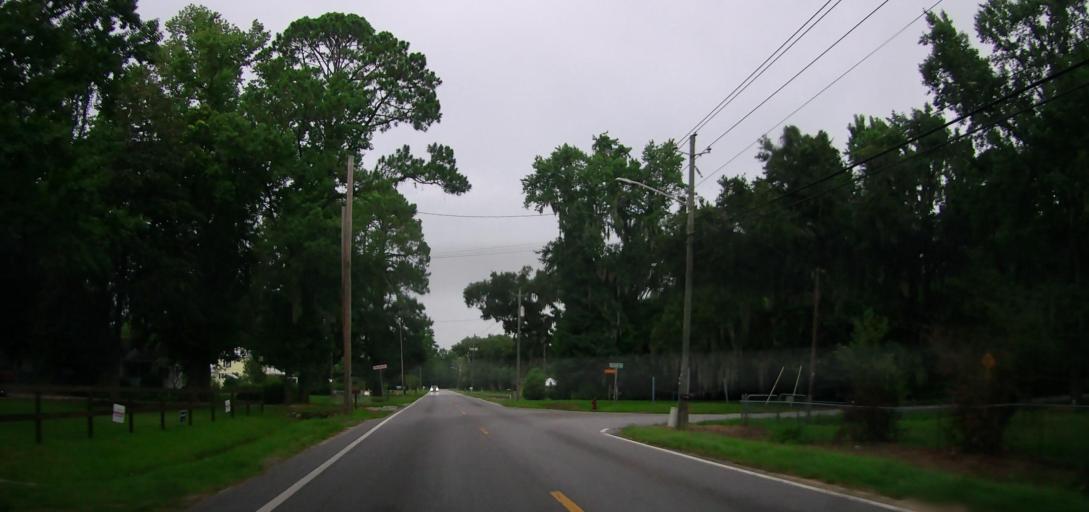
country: US
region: Georgia
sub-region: Glynn County
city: Dock Junction
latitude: 31.2256
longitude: -81.5105
